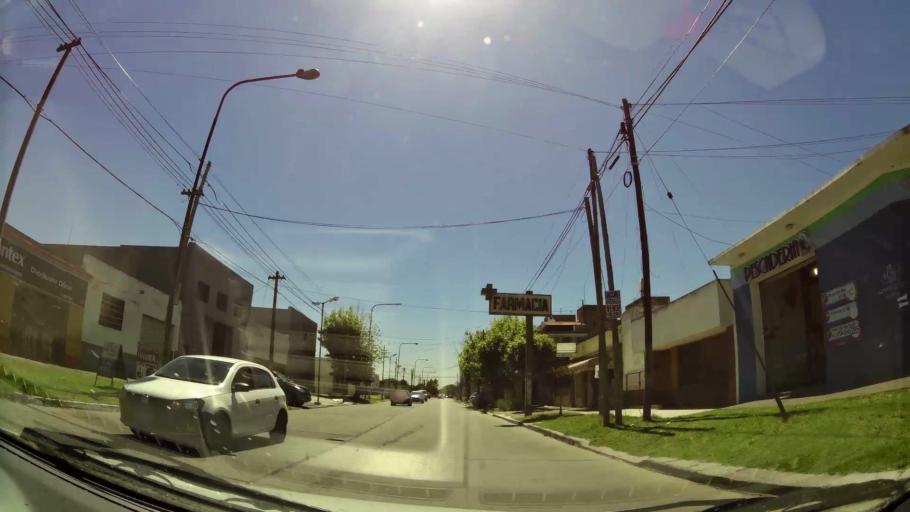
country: AR
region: Buenos Aires
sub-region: Partido de Quilmes
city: Quilmes
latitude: -34.7223
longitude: -58.2864
